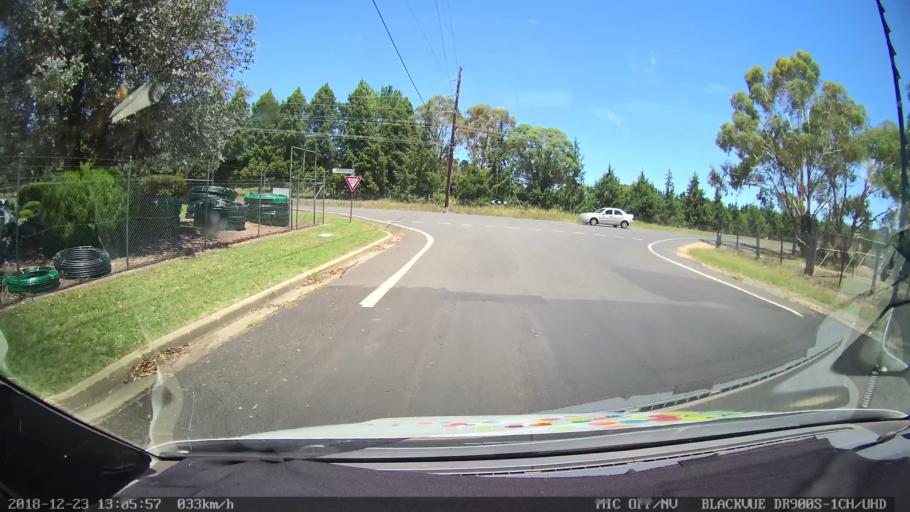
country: AU
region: New South Wales
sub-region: Armidale Dumaresq
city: Armidale
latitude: -30.5168
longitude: 151.6405
